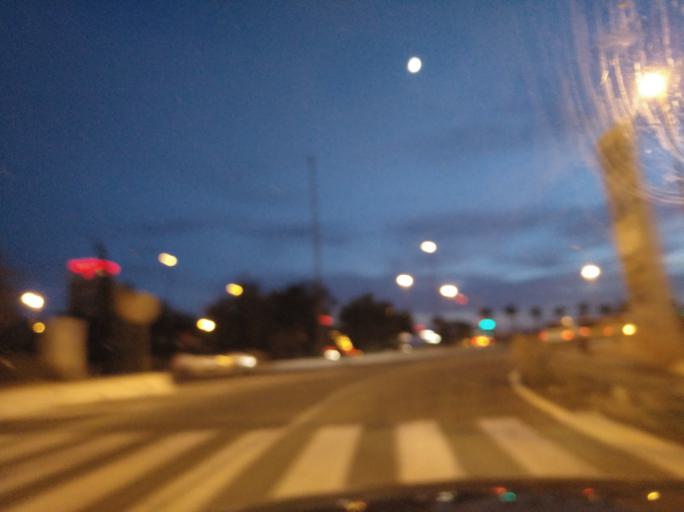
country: ES
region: Andalusia
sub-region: Provincia de Sevilla
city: Camas
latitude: 37.3902
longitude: -6.0139
